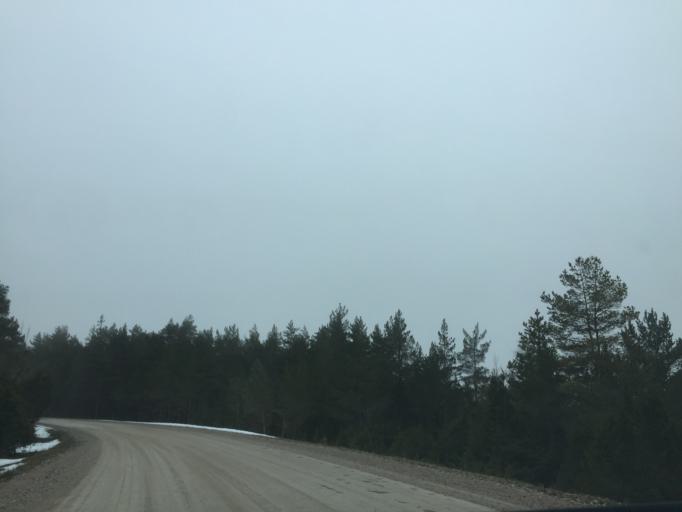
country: EE
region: Saare
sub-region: Kuressaare linn
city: Kuressaare
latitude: 58.4901
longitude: 21.9857
